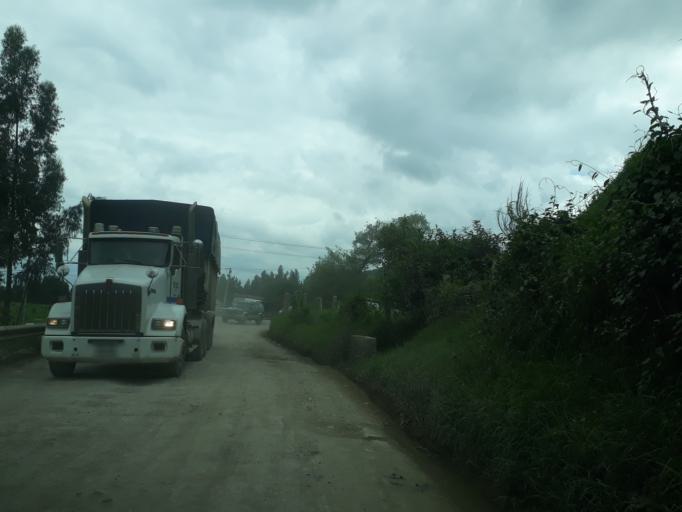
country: CO
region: Cundinamarca
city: Ubate
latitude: 5.3233
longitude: -73.7707
